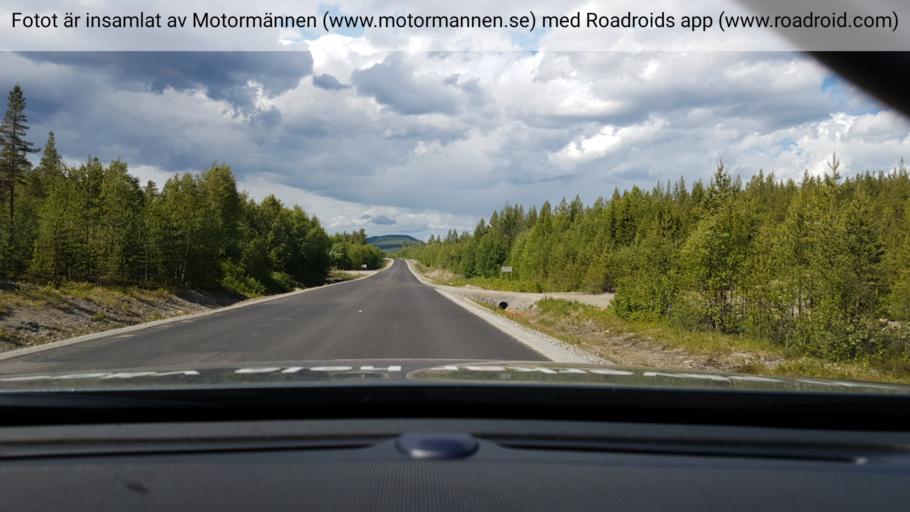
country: SE
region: Vaesterbotten
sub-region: Lycksele Kommun
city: Lycksele
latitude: 63.9905
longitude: 18.4782
